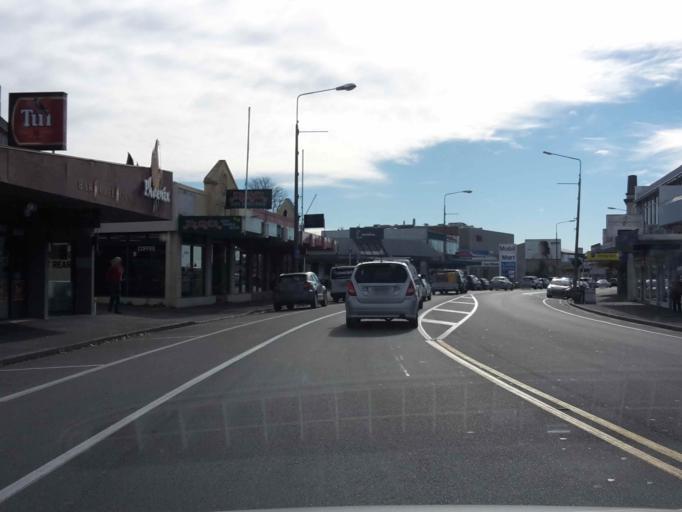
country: NZ
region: Canterbury
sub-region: Christchurch City
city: Christchurch
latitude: -43.4968
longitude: 172.6079
